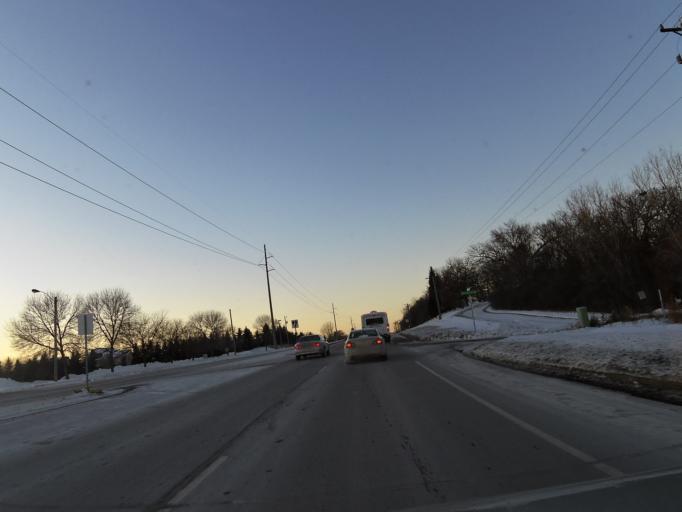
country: US
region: Minnesota
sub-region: Dakota County
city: Apple Valley
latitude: 44.7332
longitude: -93.2531
